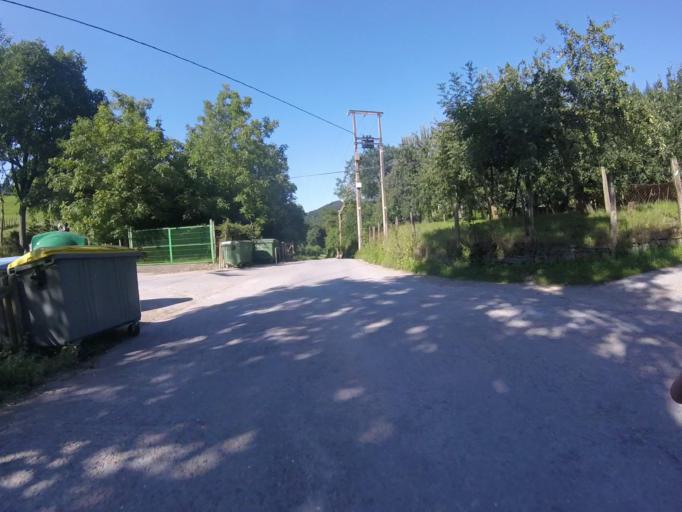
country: ES
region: Basque Country
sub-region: Provincia de Guipuzcoa
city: Irun
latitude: 43.3214
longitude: -1.7803
